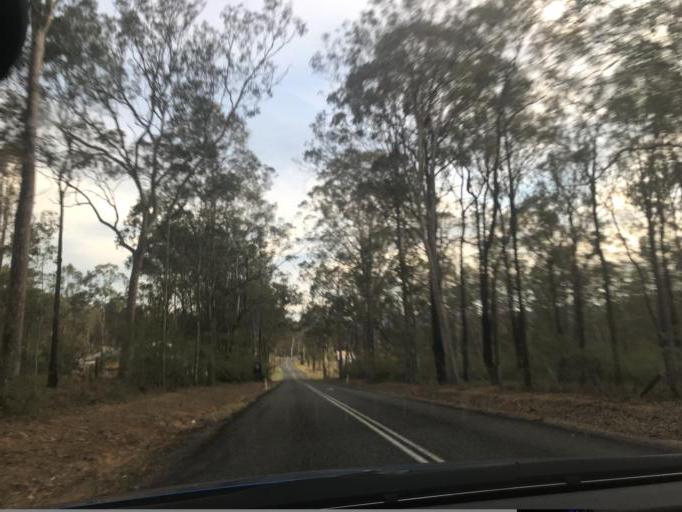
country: AU
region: New South Wales
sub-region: Cessnock
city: Cessnock
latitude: -32.8963
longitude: 151.2946
